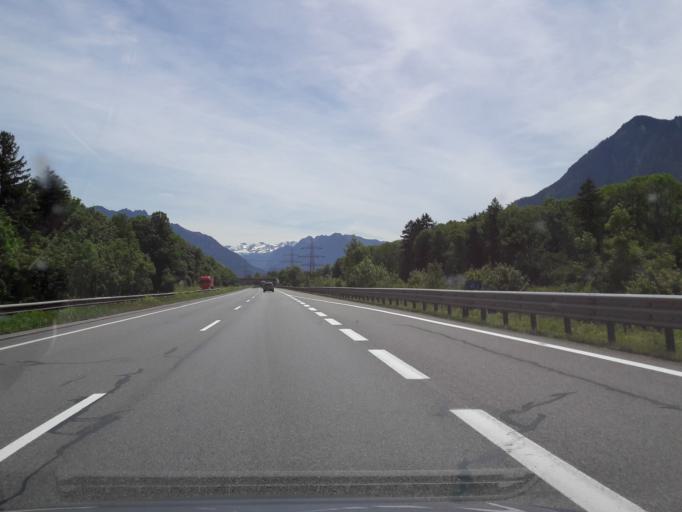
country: AT
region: Vorarlberg
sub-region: Politischer Bezirk Feldkirch
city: Schlins
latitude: 47.2000
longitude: 9.6822
